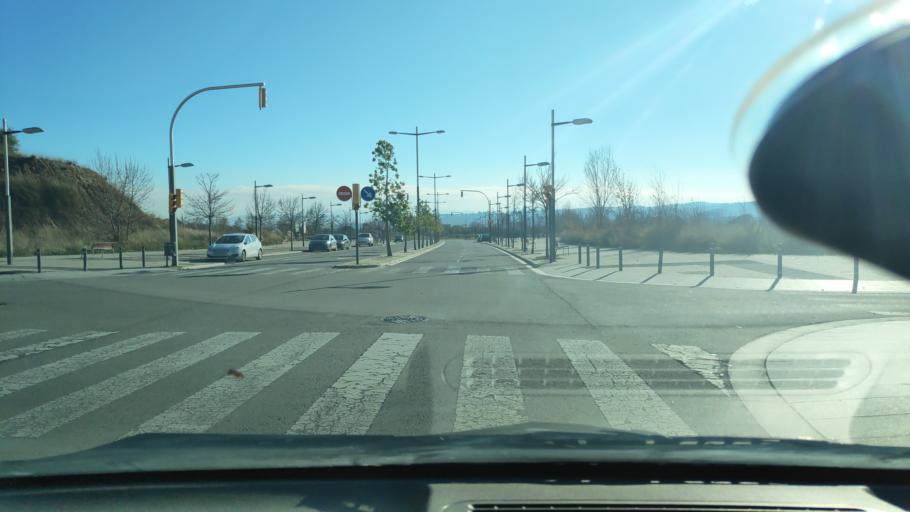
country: ES
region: Catalonia
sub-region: Provincia de Barcelona
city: Sant Quirze del Valles
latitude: 41.5490
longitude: 2.0788
